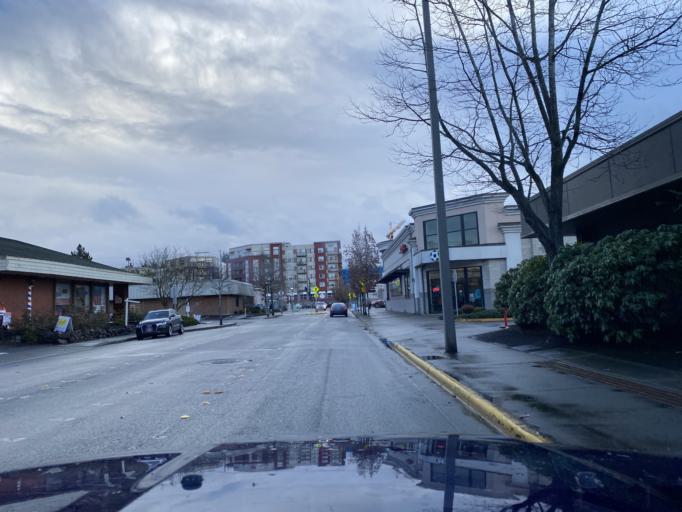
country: US
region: Washington
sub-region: King County
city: Redmond
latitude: 47.6764
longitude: -122.1275
